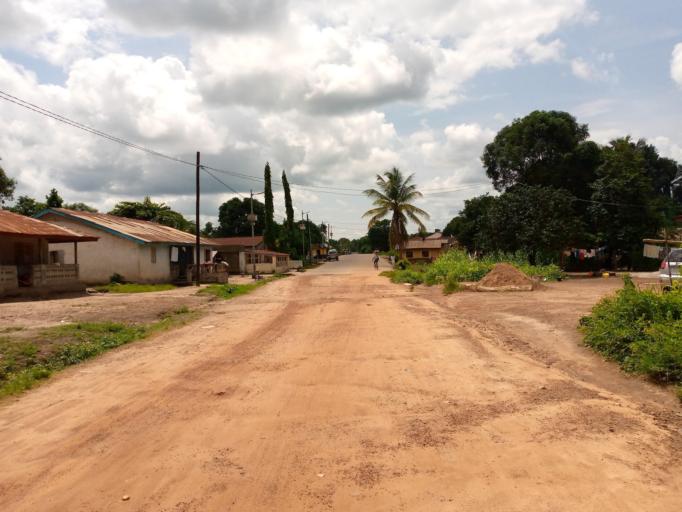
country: SL
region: Northern Province
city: Magburaka
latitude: 8.7142
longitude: -11.9363
